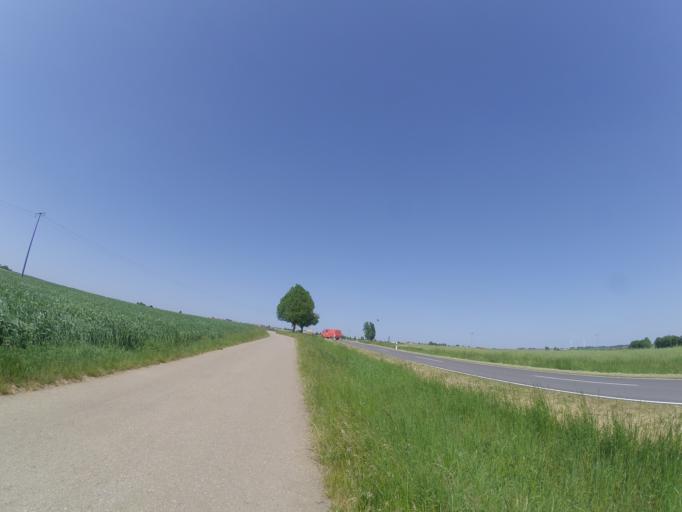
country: DE
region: Baden-Wuerttemberg
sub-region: Tuebingen Region
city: Nellingen
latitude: 48.5331
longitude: 9.7806
